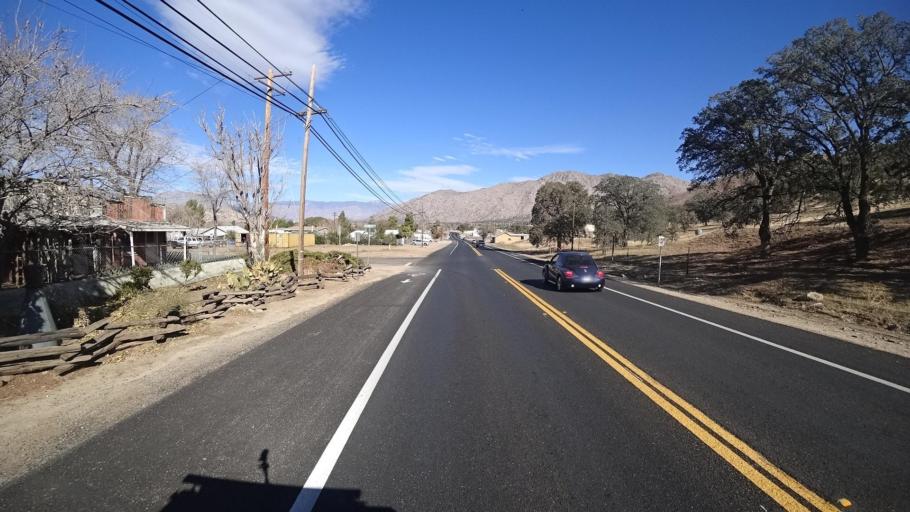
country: US
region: California
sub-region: Kern County
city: Bodfish
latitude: 35.5975
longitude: -118.4909
